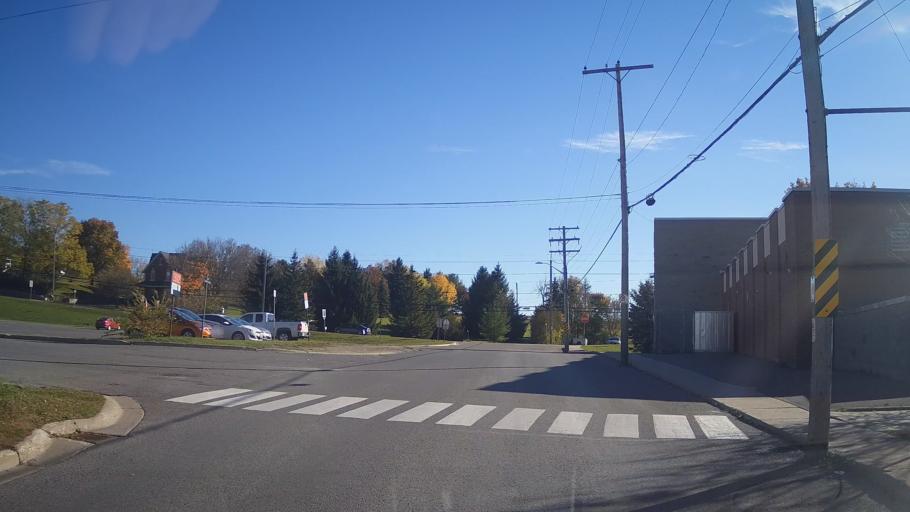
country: CA
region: Ontario
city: Kingston
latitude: 44.4079
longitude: -76.5946
